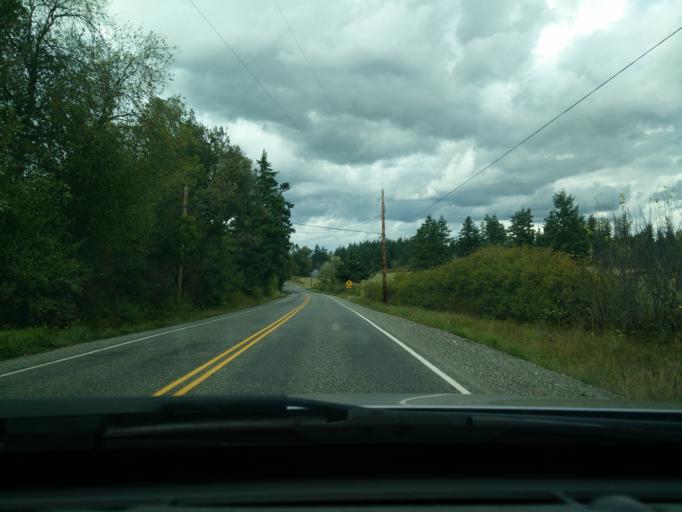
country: US
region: Washington
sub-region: Skagit County
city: Anacortes
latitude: 48.4988
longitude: -122.4817
